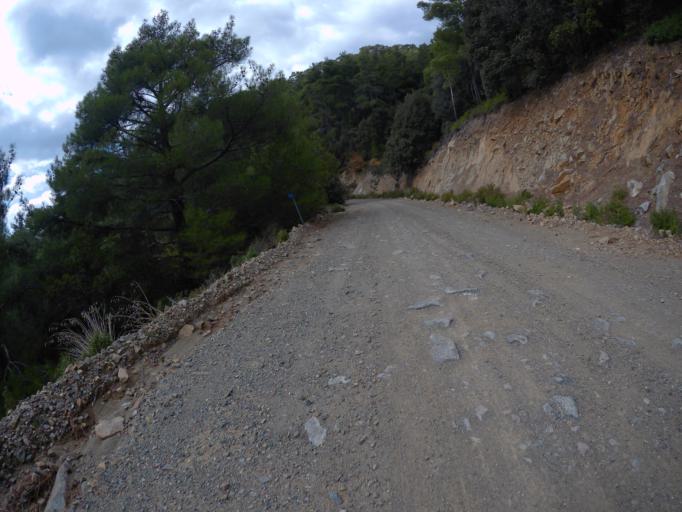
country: CY
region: Limassol
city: Pelendri
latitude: 34.8904
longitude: 32.8809
